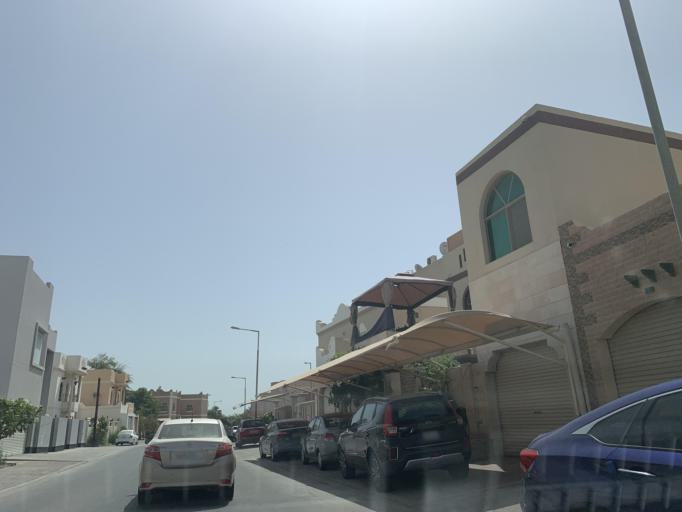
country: BH
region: Northern
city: Sitrah
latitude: 26.1542
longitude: 50.5850
